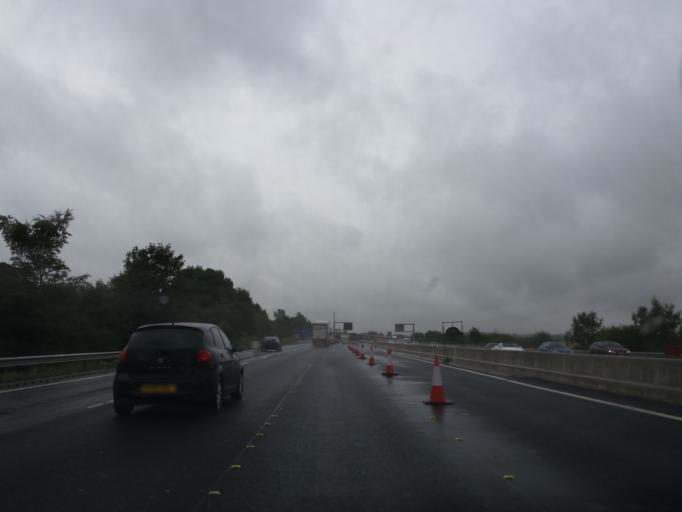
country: GB
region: England
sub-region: Rotherham
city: Wales
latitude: 53.3352
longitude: -1.2872
